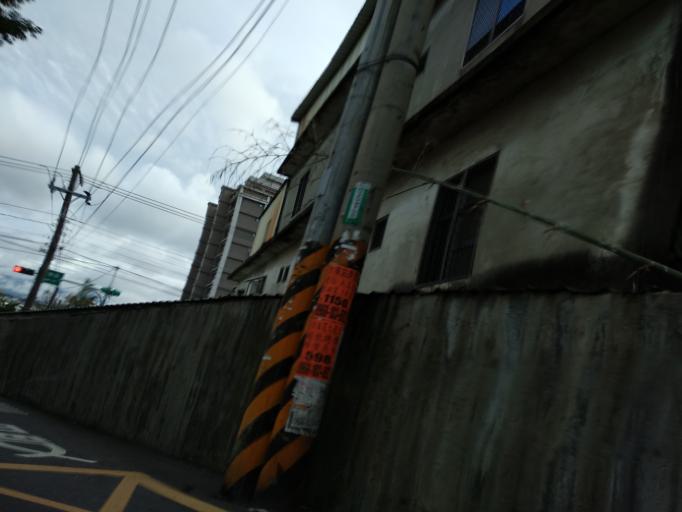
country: TW
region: Taiwan
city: Daxi
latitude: 24.9276
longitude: 121.1962
